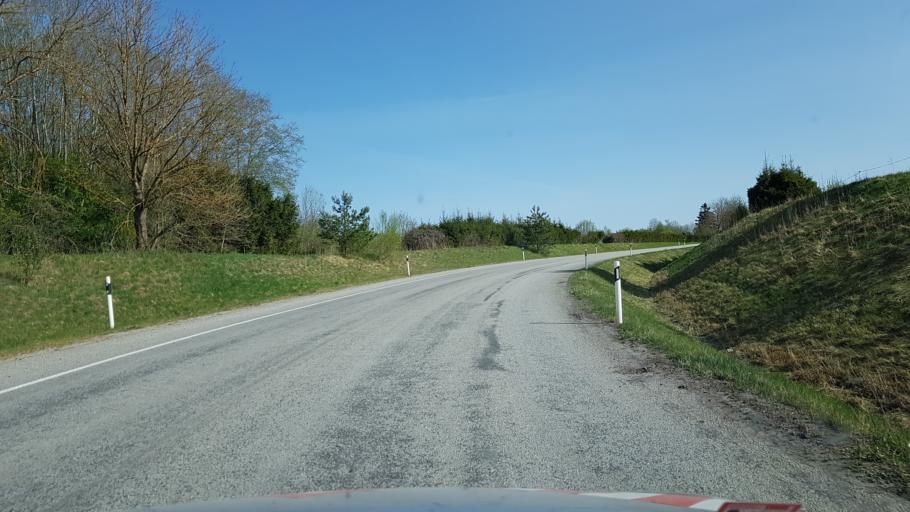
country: EE
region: Viljandimaa
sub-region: Abja vald
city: Abja-Paluoja
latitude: 58.1436
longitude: 25.3753
